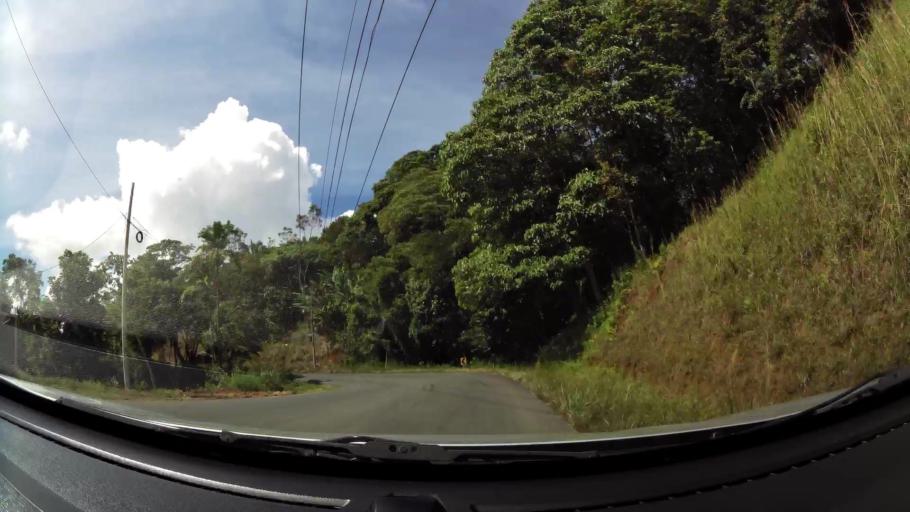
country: CR
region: San Jose
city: San Isidro
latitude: 9.3262
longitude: -83.7410
